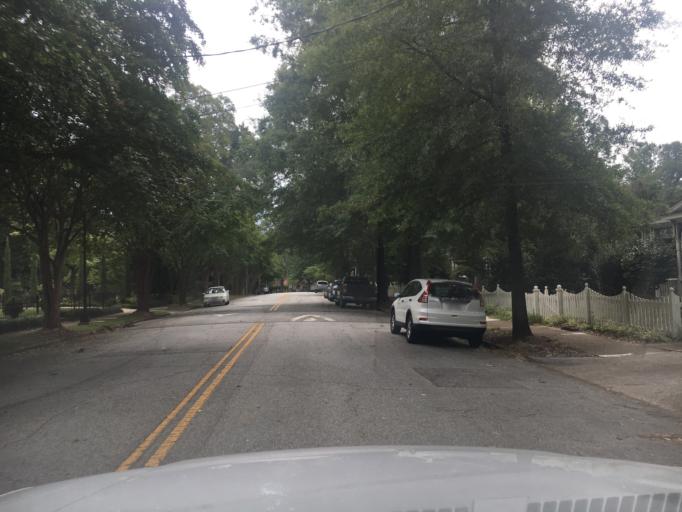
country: US
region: South Carolina
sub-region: Greenville County
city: Greenville
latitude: 34.8555
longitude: -82.4061
